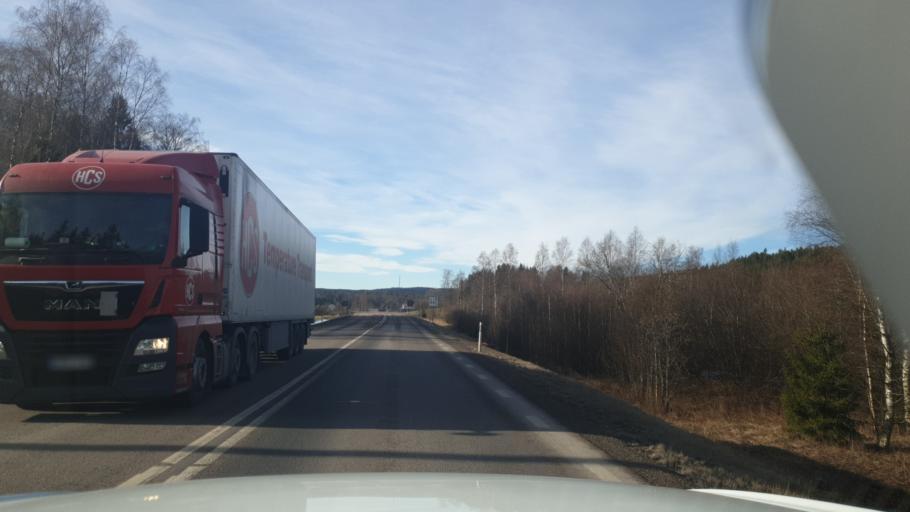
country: SE
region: Vaermland
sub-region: Arvika Kommun
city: Arvika
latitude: 59.6694
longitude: 12.8186
